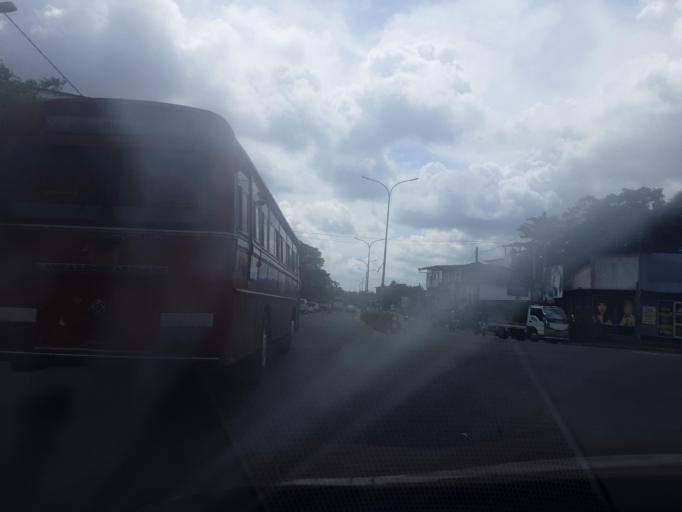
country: LK
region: North Western
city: Kuliyapitiya
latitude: 7.4701
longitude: 80.0263
